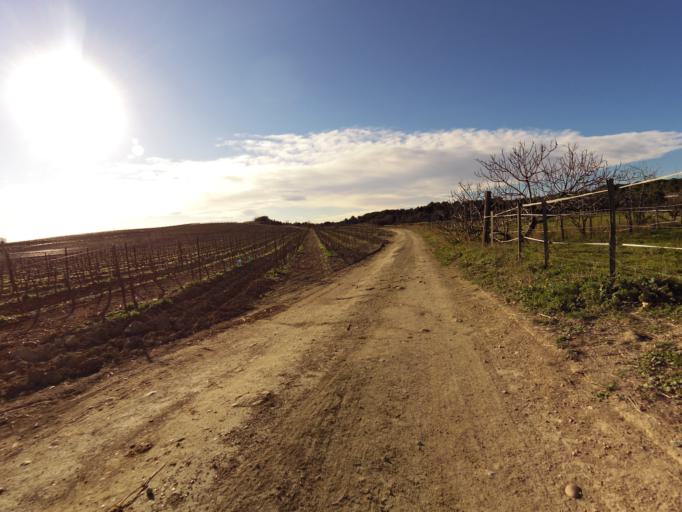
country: FR
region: Languedoc-Roussillon
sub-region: Departement du Gard
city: Mus
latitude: 43.7345
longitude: 4.1996
